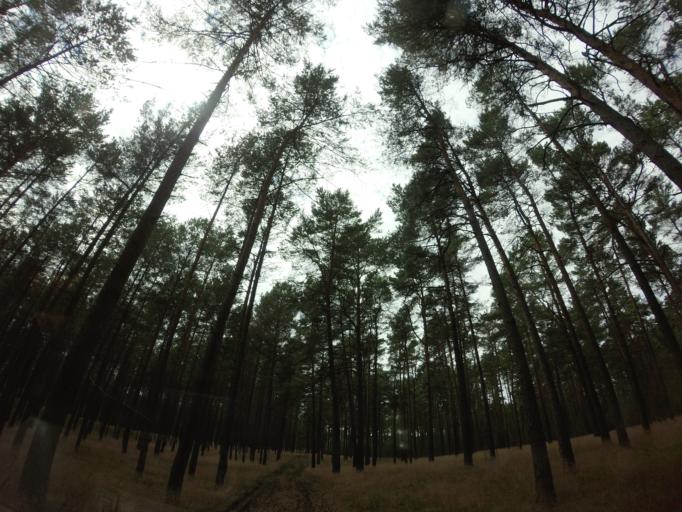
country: PL
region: West Pomeranian Voivodeship
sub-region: Powiat choszczenski
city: Drawno
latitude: 53.1584
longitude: 15.7545
